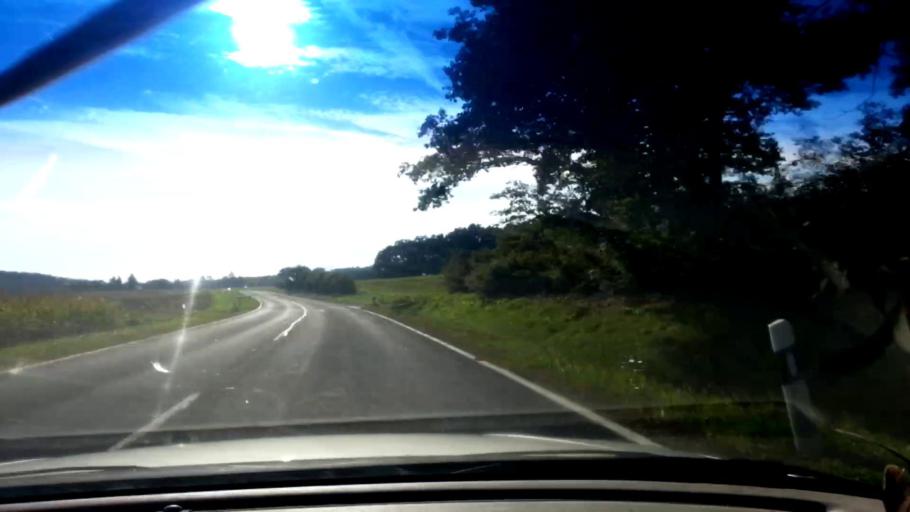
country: DE
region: Bavaria
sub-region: Upper Franconia
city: Baunach
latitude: 49.9806
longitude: 10.8294
